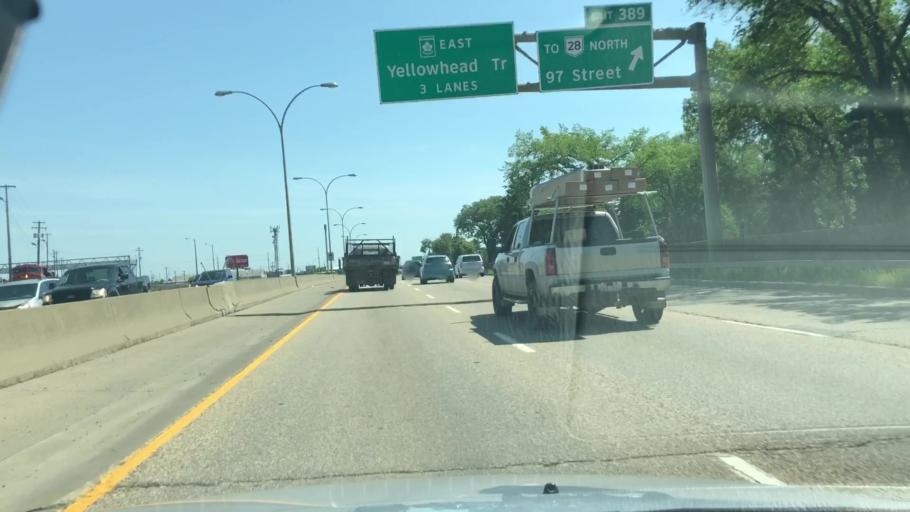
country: CA
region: Alberta
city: Edmonton
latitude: 53.5814
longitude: -113.5012
